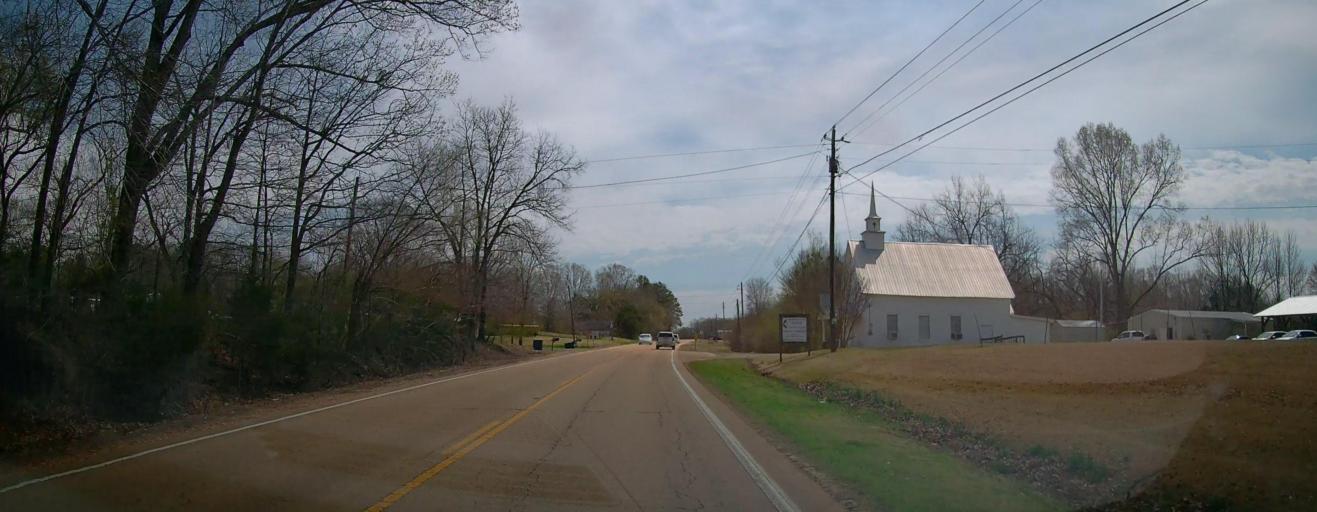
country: US
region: Mississippi
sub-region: Marshall County
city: Holly Springs
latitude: 34.6321
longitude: -89.2752
